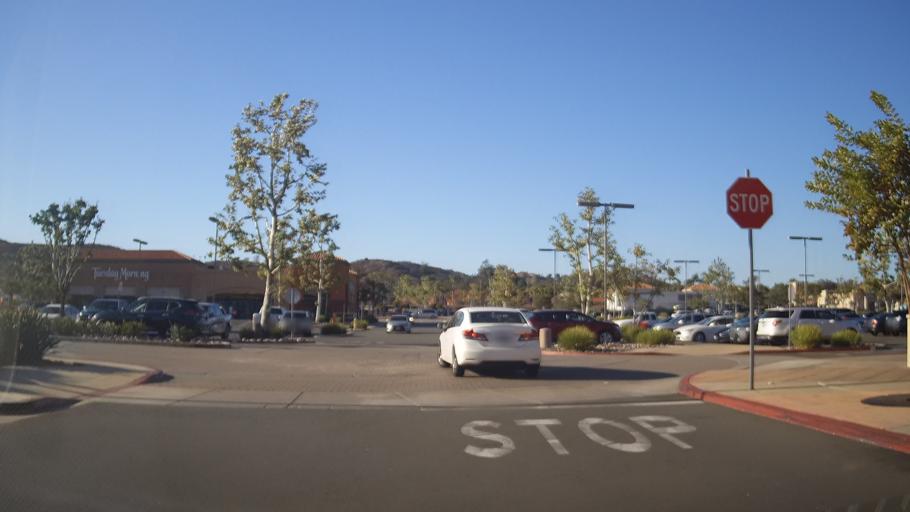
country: US
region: California
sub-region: San Diego County
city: Rancho San Diego
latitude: 32.7375
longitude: -116.9403
